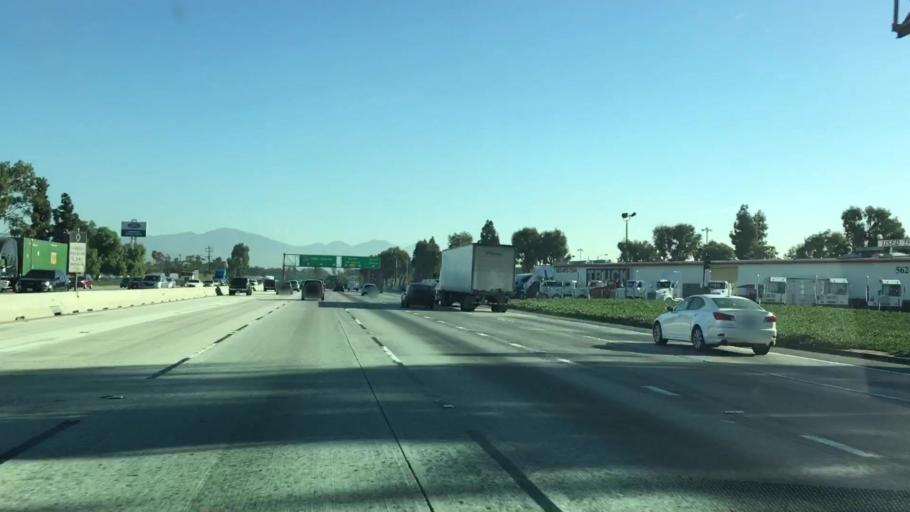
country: US
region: California
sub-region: Los Angeles County
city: South El Monte
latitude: 34.0278
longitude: -118.0365
